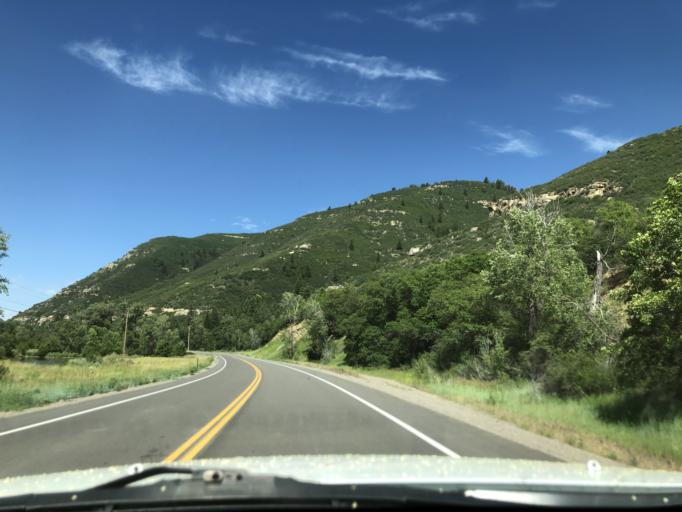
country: US
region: Colorado
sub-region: Delta County
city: Paonia
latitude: 38.9385
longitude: -107.3781
